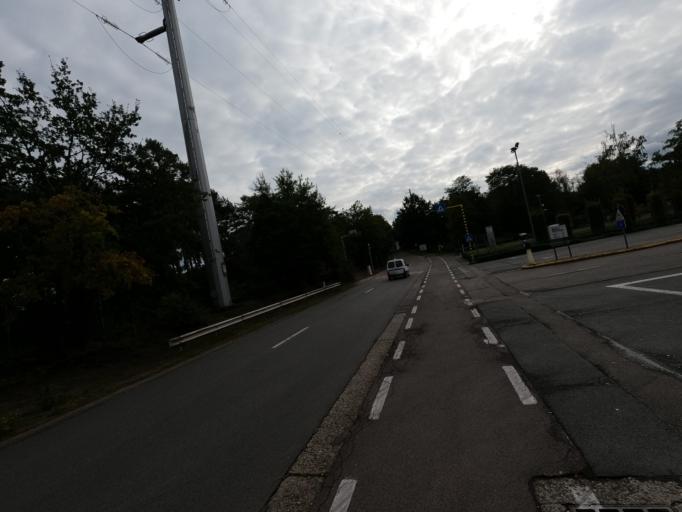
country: BE
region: Flanders
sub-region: Provincie Antwerpen
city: Dessel
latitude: 51.2256
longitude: 5.0928
